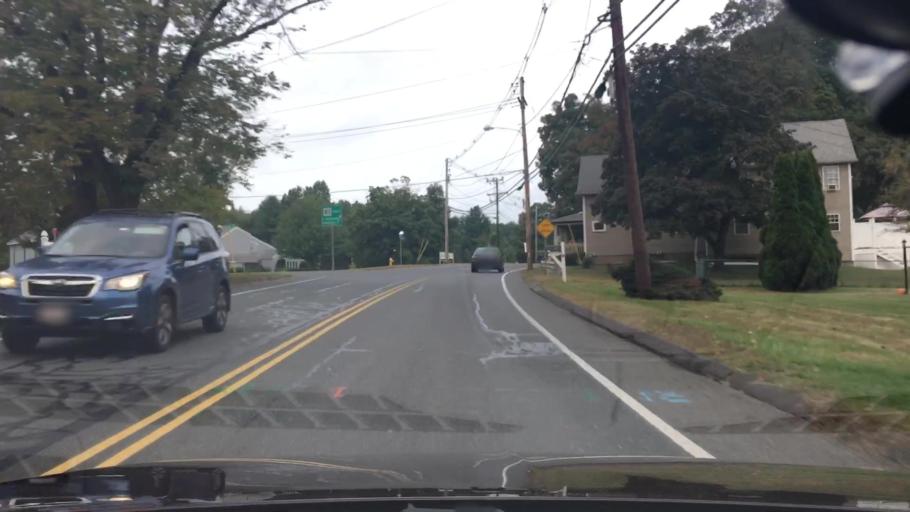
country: US
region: Massachusetts
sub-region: Hampden County
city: East Longmeadow
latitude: 42.0560
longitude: -72.4997
